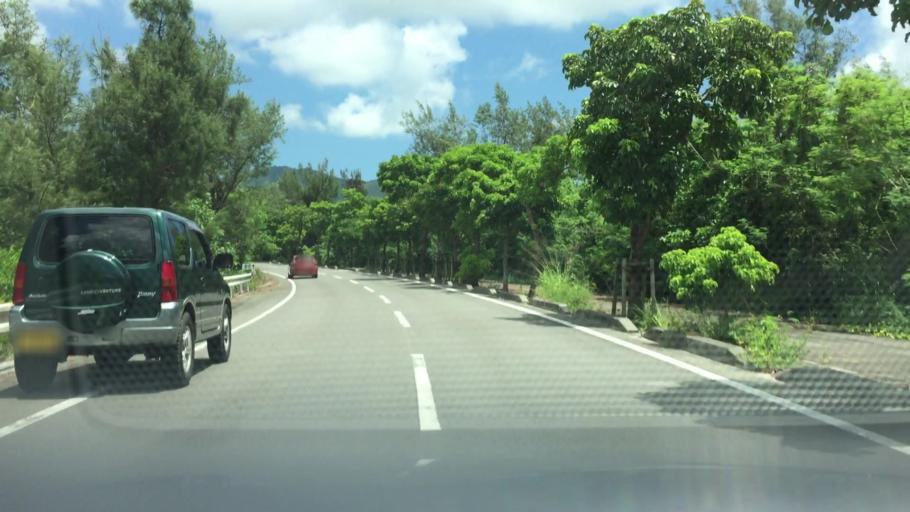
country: JP
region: Okinawa
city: Ishigaki
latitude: 24.3930
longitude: 124.1419
